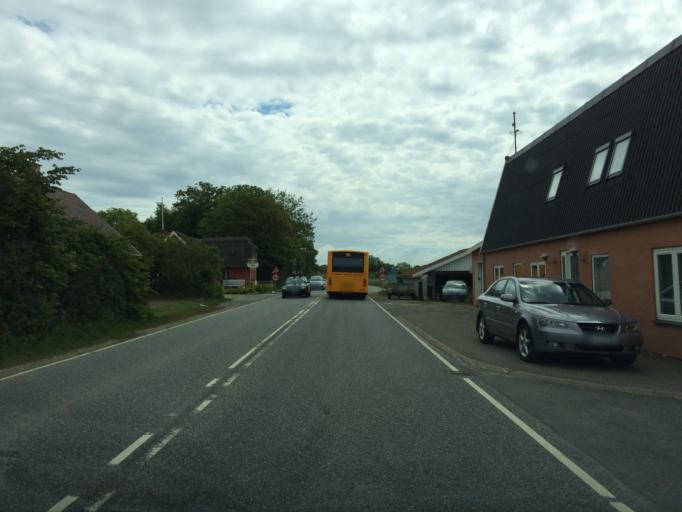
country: DK
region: Zealand
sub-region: Odsherred Kommune
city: Hojby
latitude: 55.9489
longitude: 11.4941
